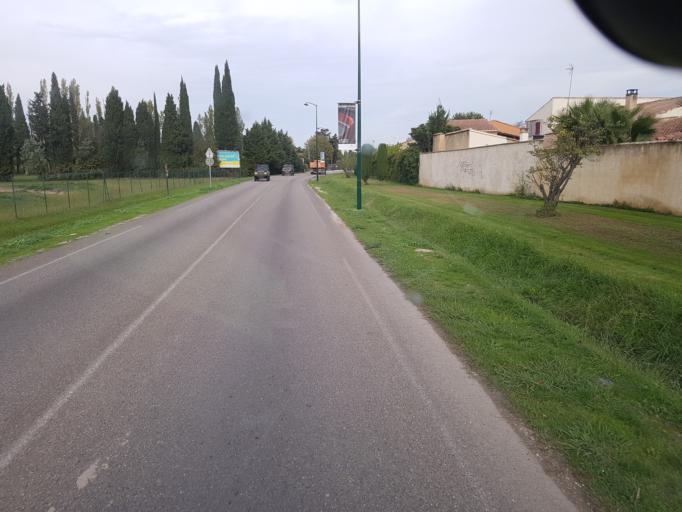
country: FR
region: Provence-Alpes-Cote d'Azur
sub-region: Departement des Bouches-du-Rhone
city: Barbentane
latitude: 43.9010
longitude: 4.7432
